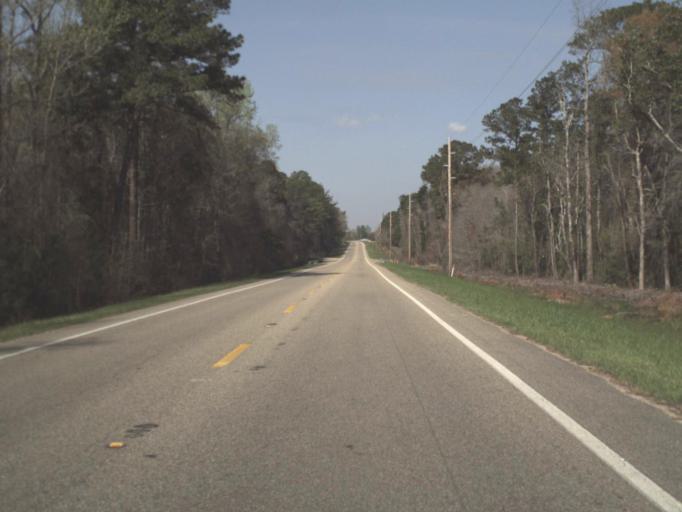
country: US
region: Florida
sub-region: Liberty County
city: Bristol
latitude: 30.4284
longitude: -84.9330
